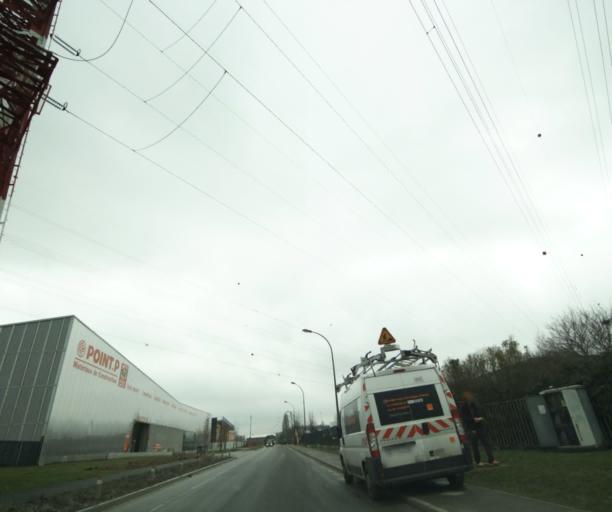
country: FR
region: Ile-de-France
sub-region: Departement de l'Essonne
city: Massy
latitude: 48.7216
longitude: 2.2804
